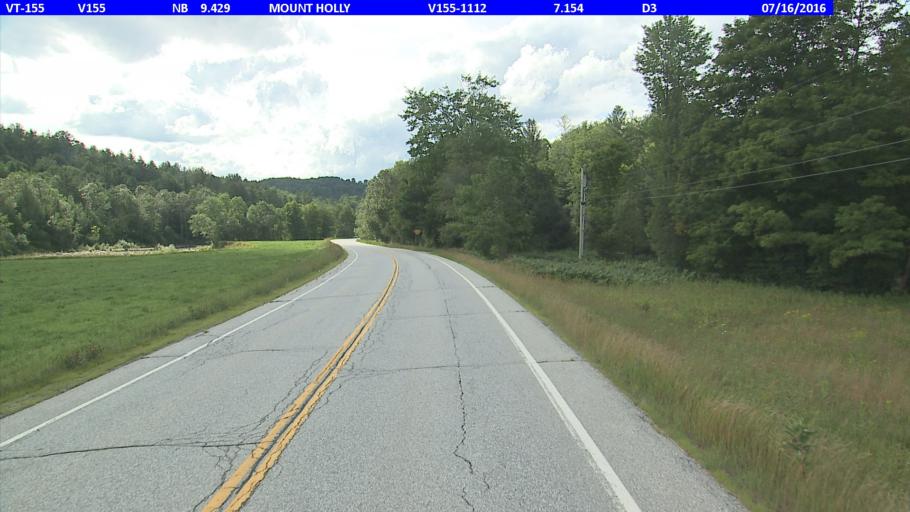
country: US
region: Vermont
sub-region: Rutland County
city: Rutland
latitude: 43.4430
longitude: -72.8676
